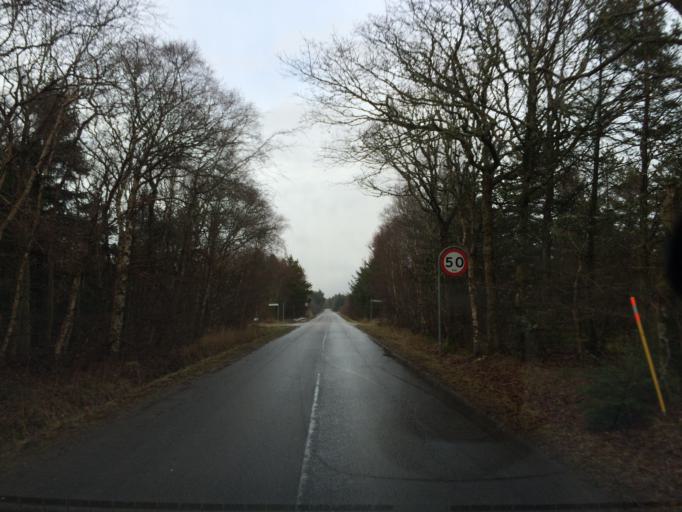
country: DK
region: Central Jutland
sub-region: Holstebro Kommune
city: Ulfborg
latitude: 56.2643
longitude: 8.1512
